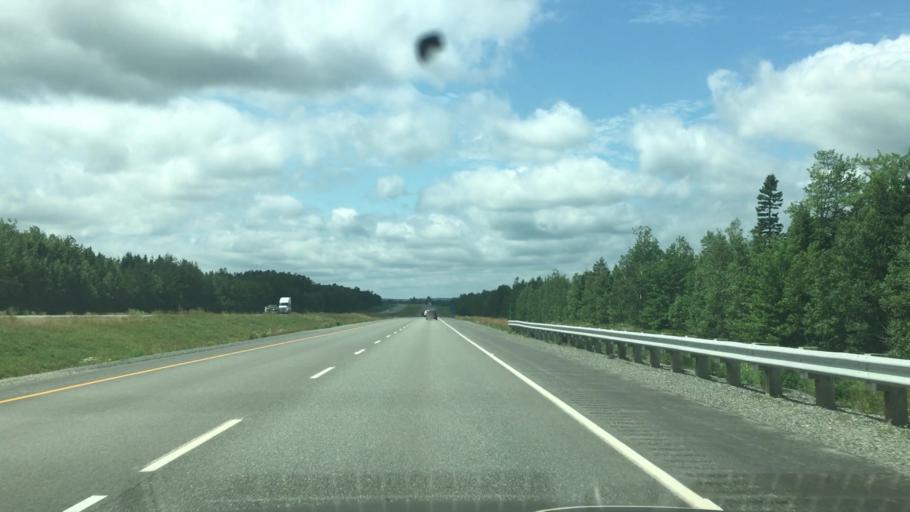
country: CA
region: Nova Scotia
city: Oxford
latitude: 45.7093
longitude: -63.9580
